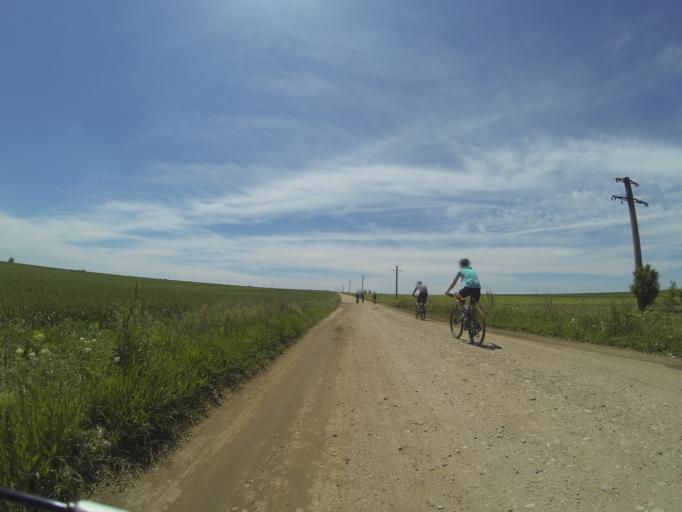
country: RO
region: Dolj
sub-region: Comuna Leu
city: Zanoaga
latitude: 44.1716
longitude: 24.0915
